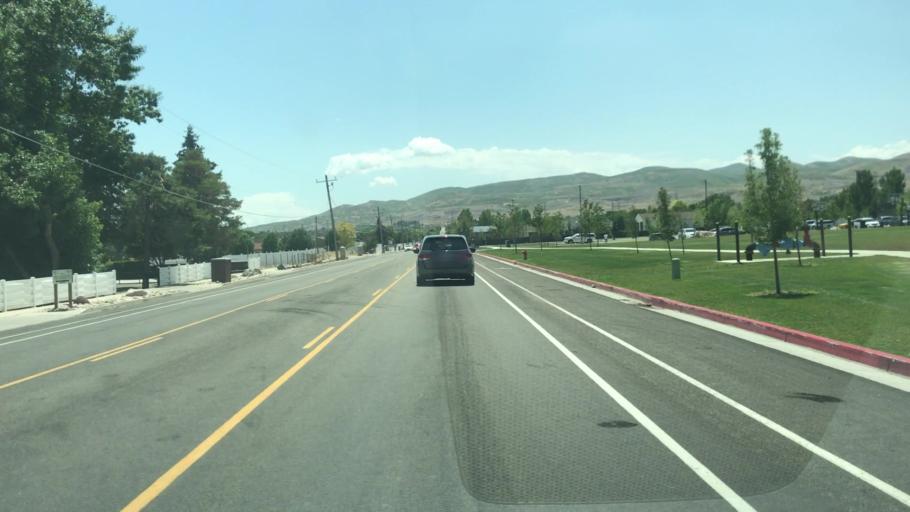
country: US
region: Utah
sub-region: Salt Lake County
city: Bluffdale
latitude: 40.4957
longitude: -111.9578
